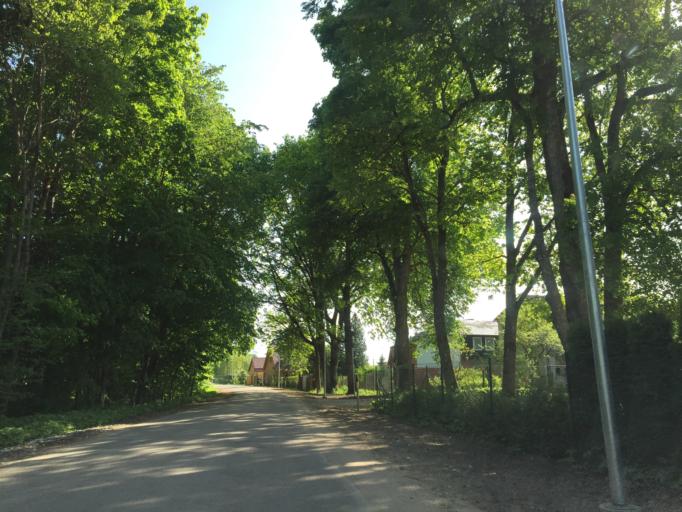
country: LV
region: Salaspils
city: Salaspils
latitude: 56.8248
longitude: 24.4283
